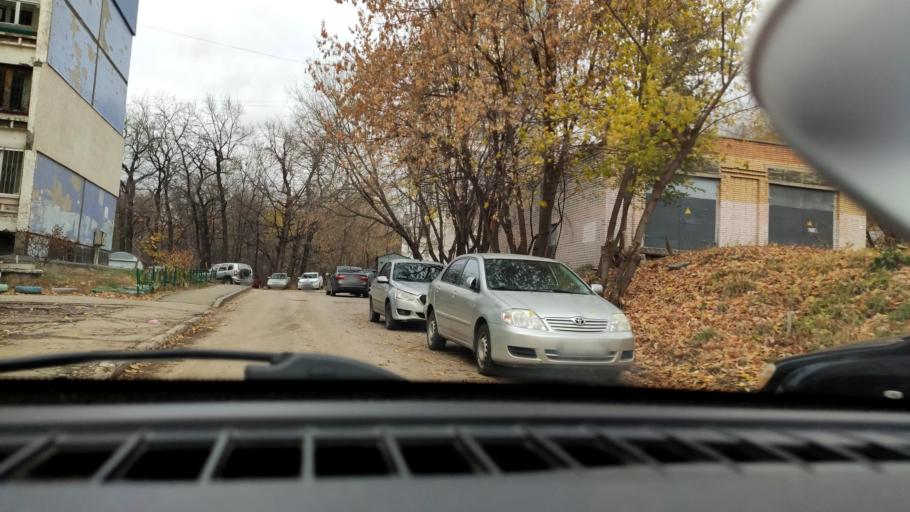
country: RU
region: Samara
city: Samara
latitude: 53.2405
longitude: 50.1916
